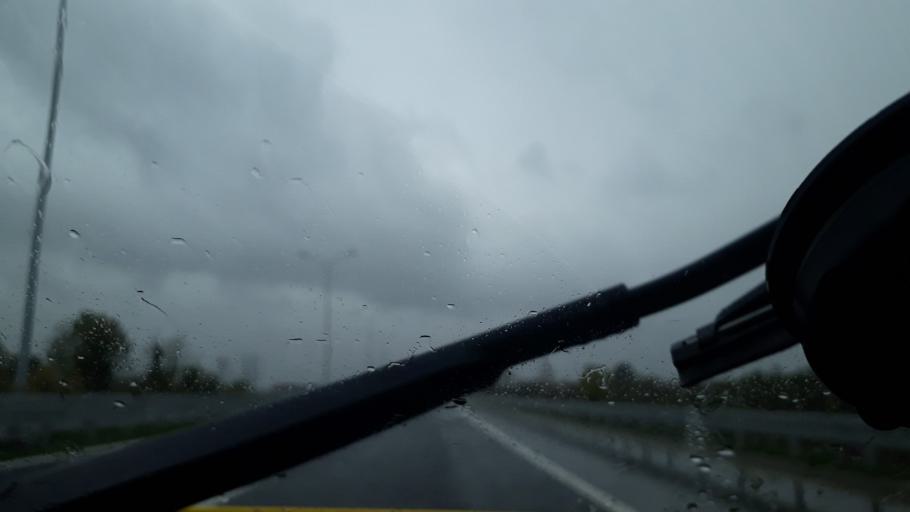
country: BA
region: Republika Srpska
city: Maglajani
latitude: 44.9100
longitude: 17.3442
